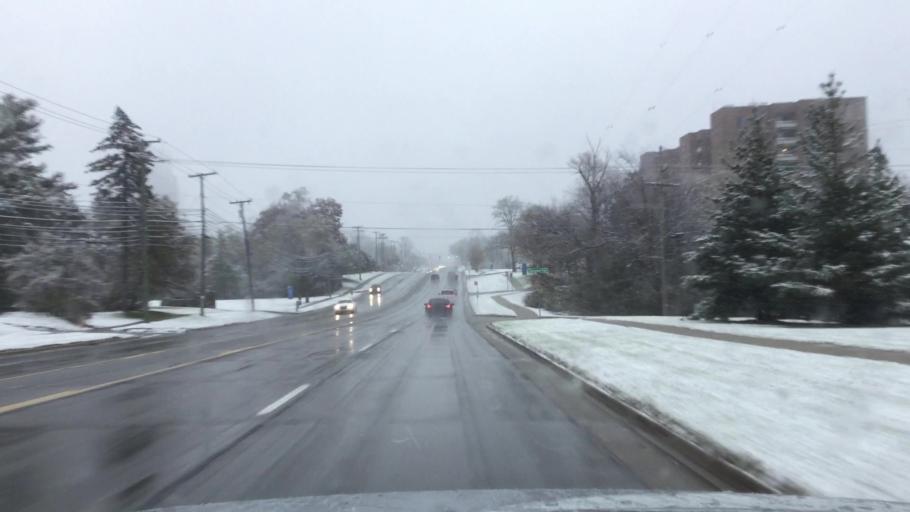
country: US
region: Michigan
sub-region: Oakland County
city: Southfield
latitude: 42.4726
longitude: -83.2543
